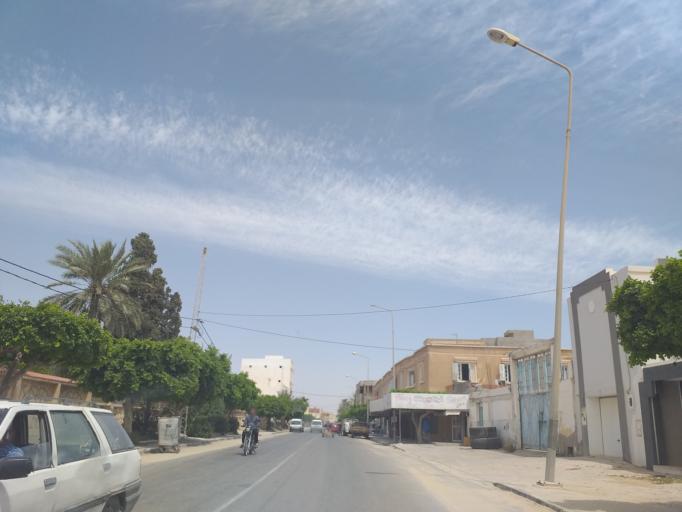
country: TN
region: Qabis
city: Gabes
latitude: 33.9322
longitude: 10.0717
